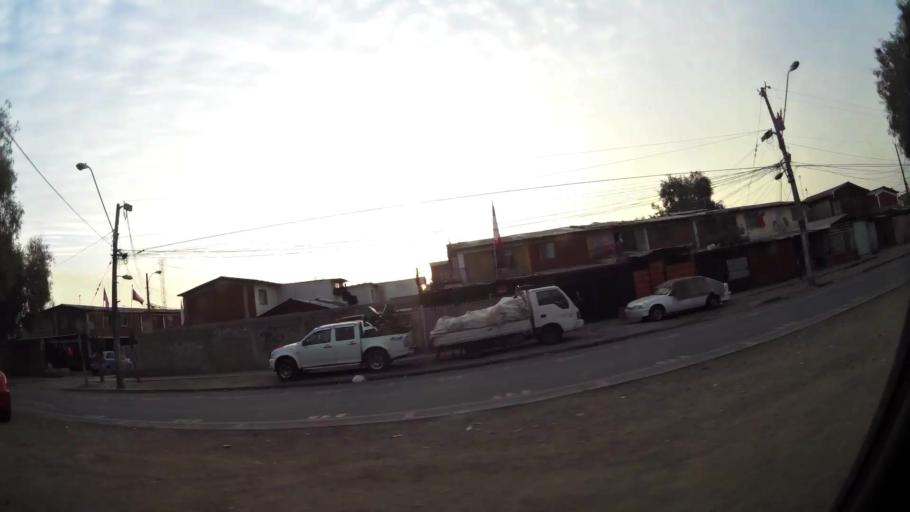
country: CL
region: Santiago Metropolitan
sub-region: Provincia de Santiago
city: Lo Prado
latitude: -33.5151
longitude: -70.7854
